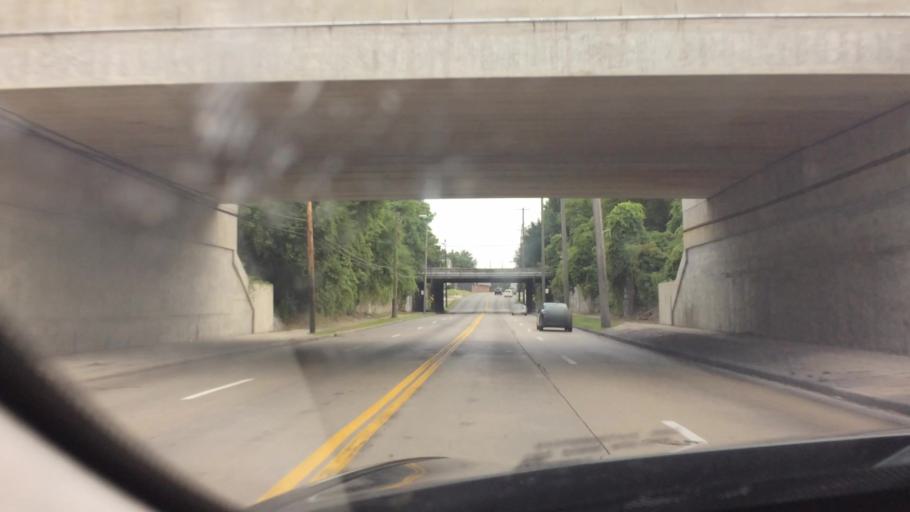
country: US
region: Ohio
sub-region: Wood County
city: Rossford
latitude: 41.6377
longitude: -83.5911
